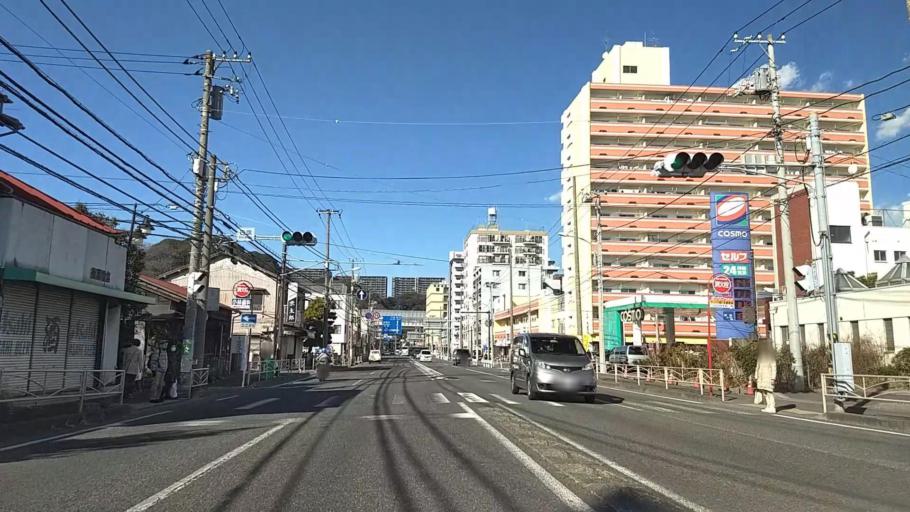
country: JP
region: Kanagawa
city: Yokohama
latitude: 35.3935
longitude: 139.6143
